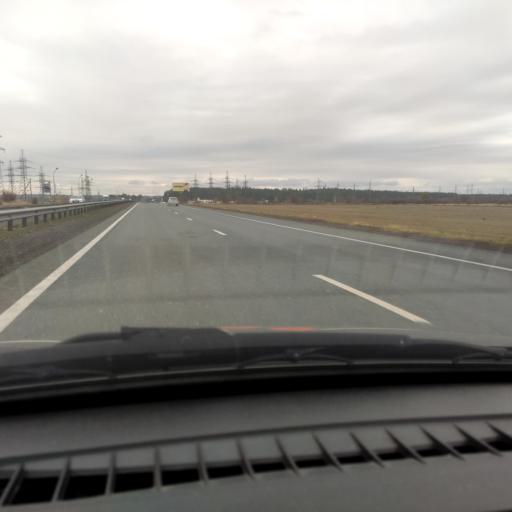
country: RU
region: Samara
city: Zhigulevsk
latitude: 53.5474
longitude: 49.5099
